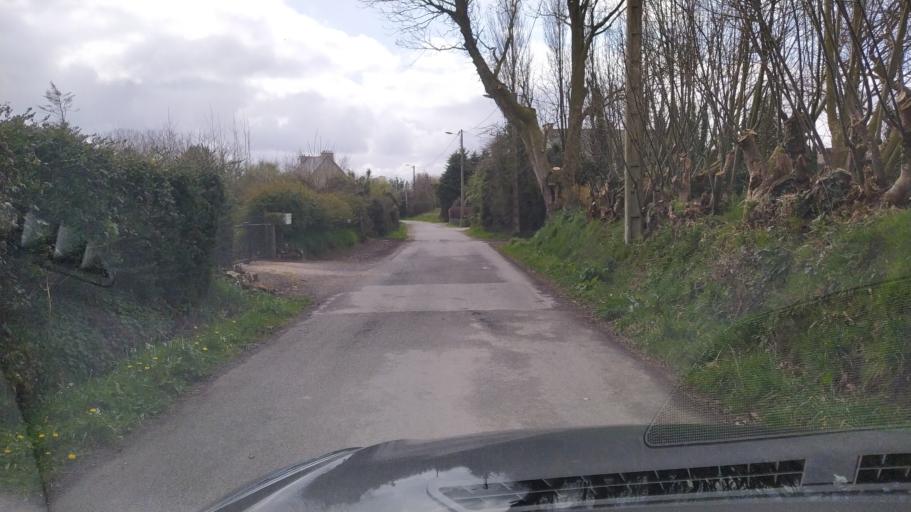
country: FR
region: Brittany
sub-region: Departement du Finistere
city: Bodilis
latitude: 48.5298
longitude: -4.1192
